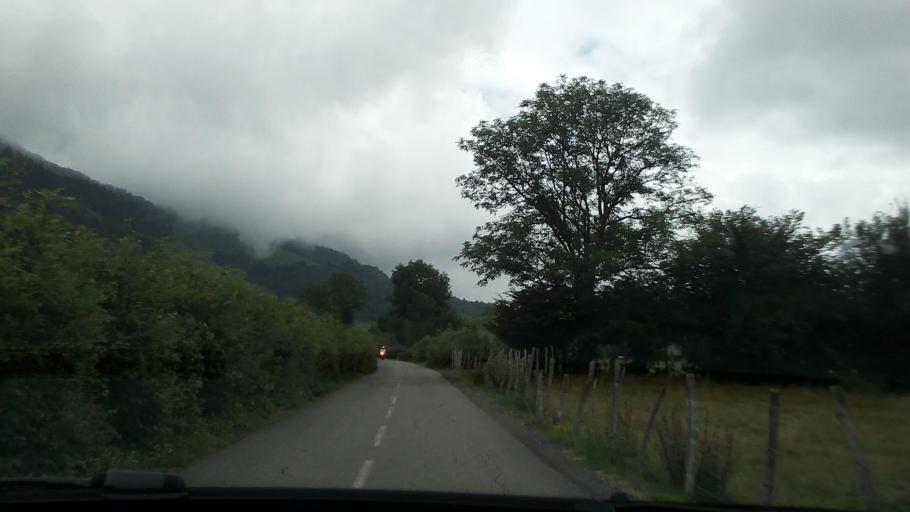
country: FR
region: Aquitaine
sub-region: Departement des Pyrenees-Atlantiques
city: Louvie-Juzon
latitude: 43.0622
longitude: -0.4759
